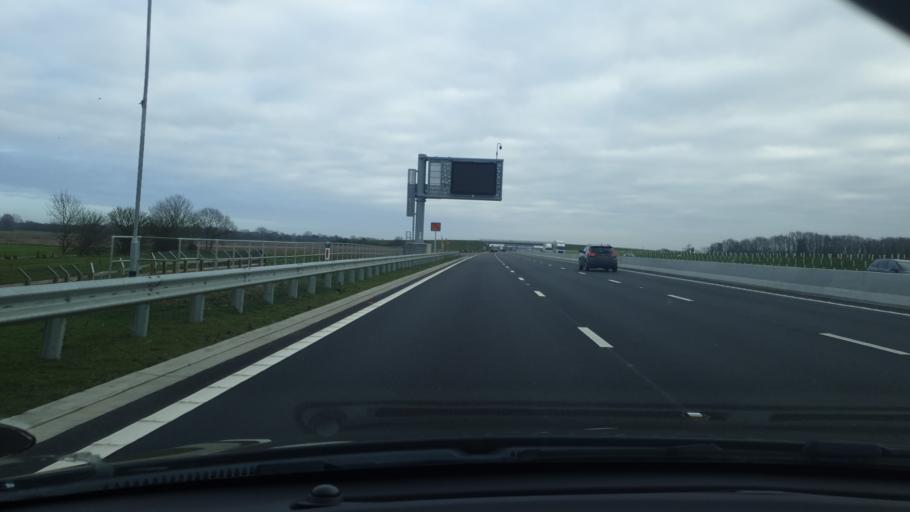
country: GB
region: England
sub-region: Cambridgeshire
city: Hemingford Grey
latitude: 52.2928
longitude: -0.1102
